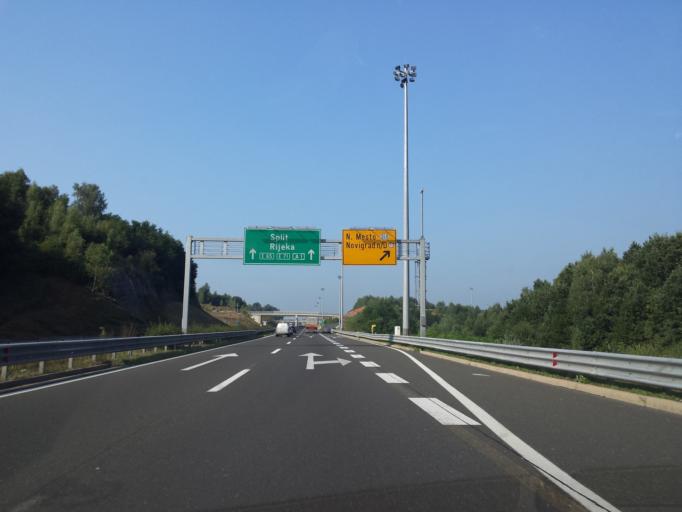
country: HR
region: Karlovacka
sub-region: Grad Karlovac
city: Karlovac
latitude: 45.4821
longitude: 15.4326
